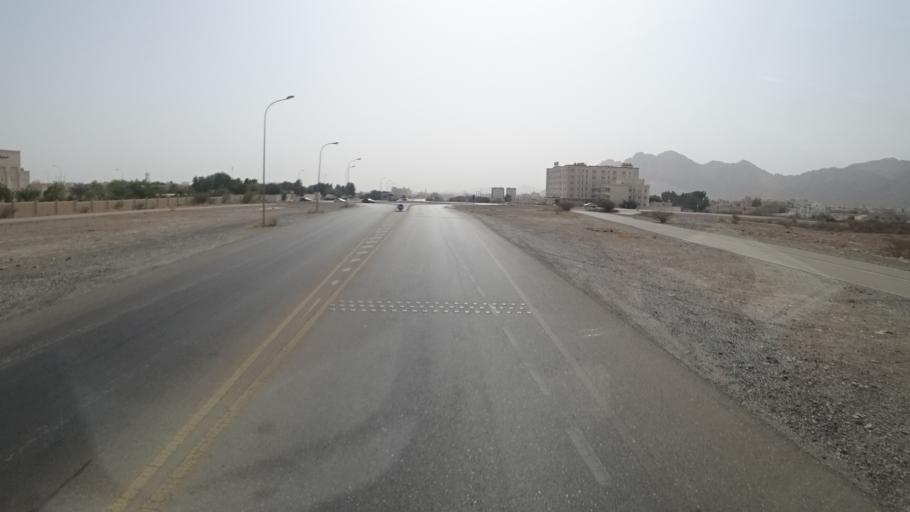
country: OM
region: Muhafazat ad Dakhiliyah
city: Nizwa
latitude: 22.9055
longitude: 57.5855
